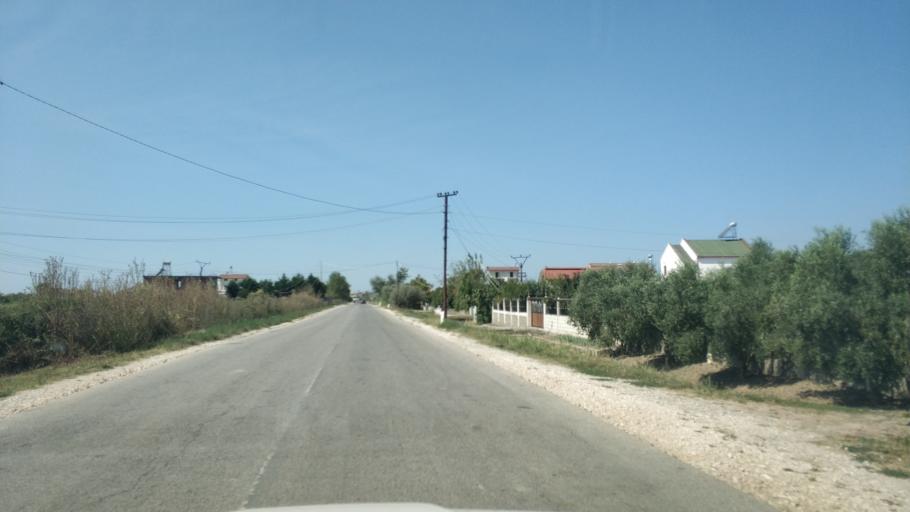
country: AL
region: Fier
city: Terbuf
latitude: 41.0520
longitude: 19.5886
